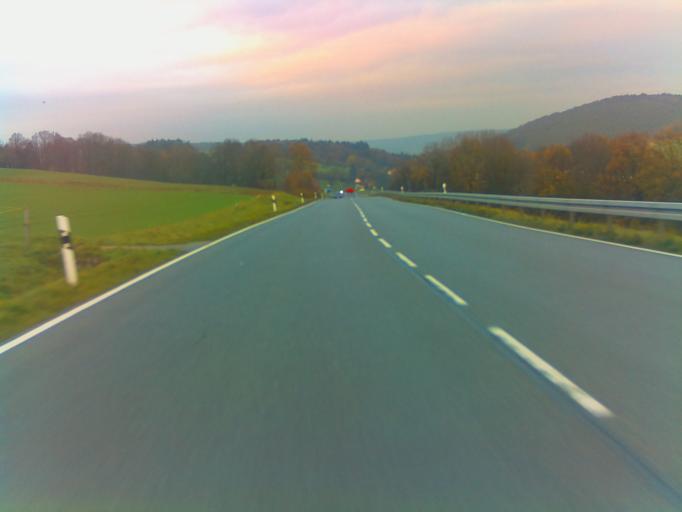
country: DE
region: Hesse
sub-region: Regierungsbezirk Darmstadt
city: Beerfelden
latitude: 49.5791
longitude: 8.9844
